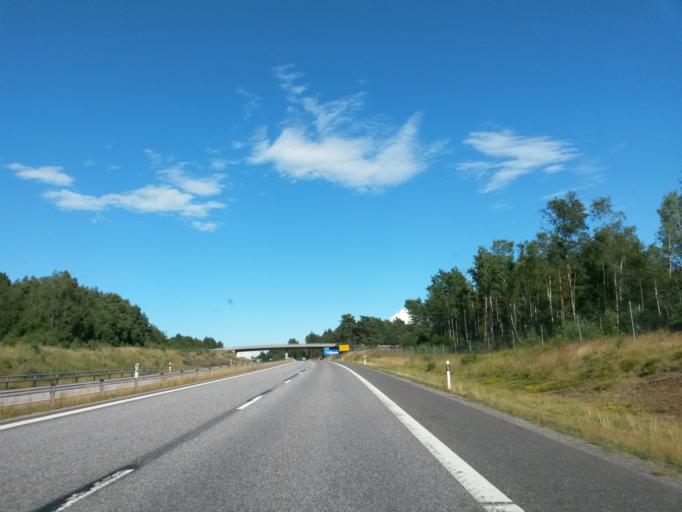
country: SE
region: Vaestra Goetaland
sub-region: Trollhattan
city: Trollhattan
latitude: 58.3341
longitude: 12.2136
